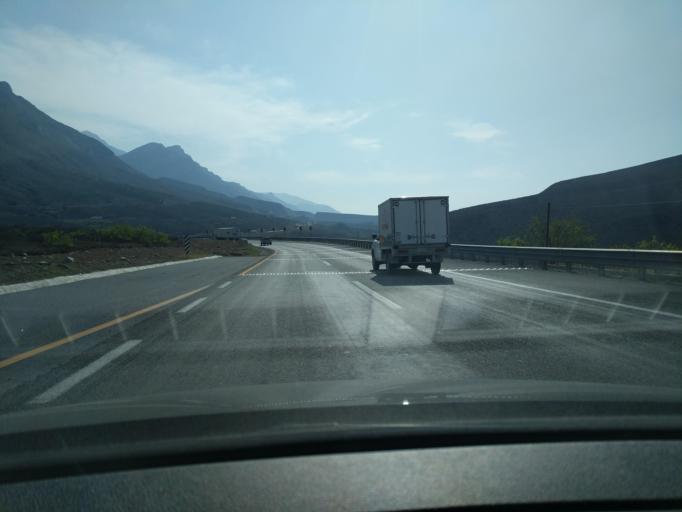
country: MX
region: Nuevo Leon
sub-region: Garcia
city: Las Torres de Guadalupe
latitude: 25.6582
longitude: -100.7184
